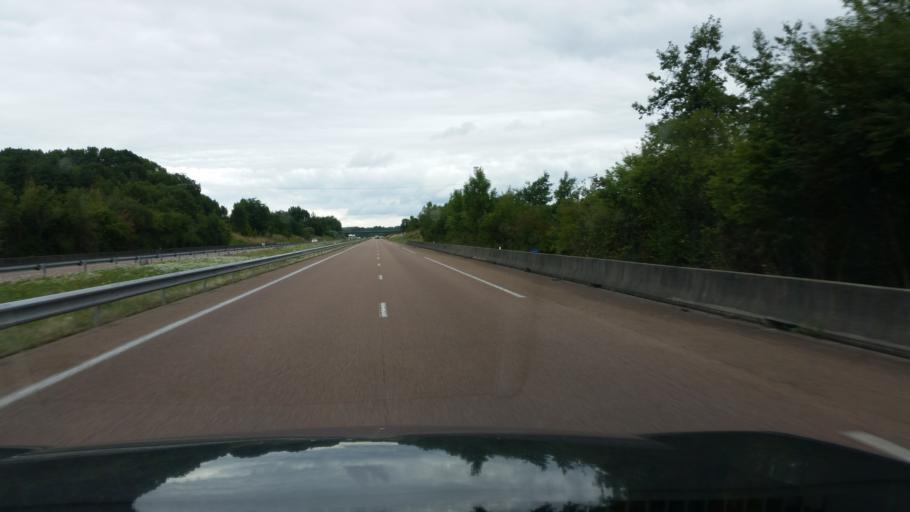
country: FR
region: Franche-Comte
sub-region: Departement du Jura
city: Bletterans
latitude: 46.7300
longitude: 5.5078
